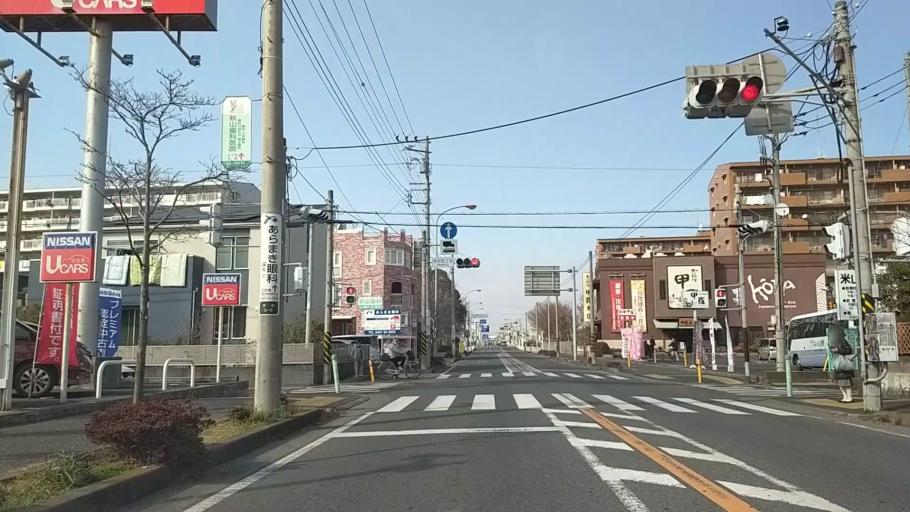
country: JP
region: Kanagawa
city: Chigasaki
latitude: 35.3386
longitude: 139.4136
